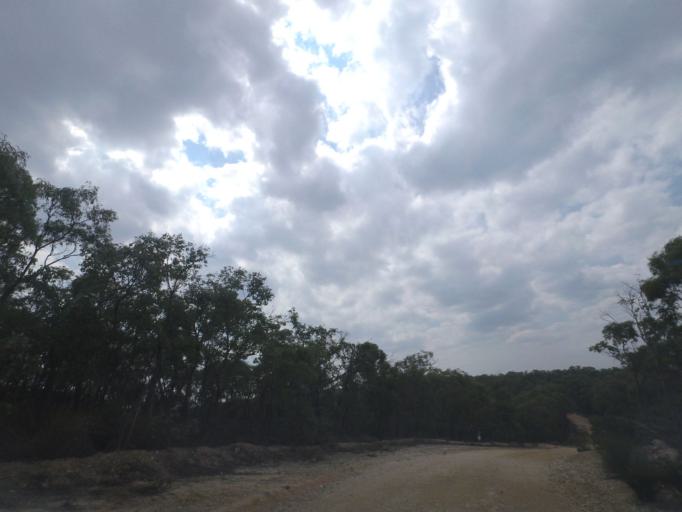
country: AU
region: Victoria
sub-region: Moorabool
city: Bacchus Marsh
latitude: -37.5490
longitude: 144.4248
